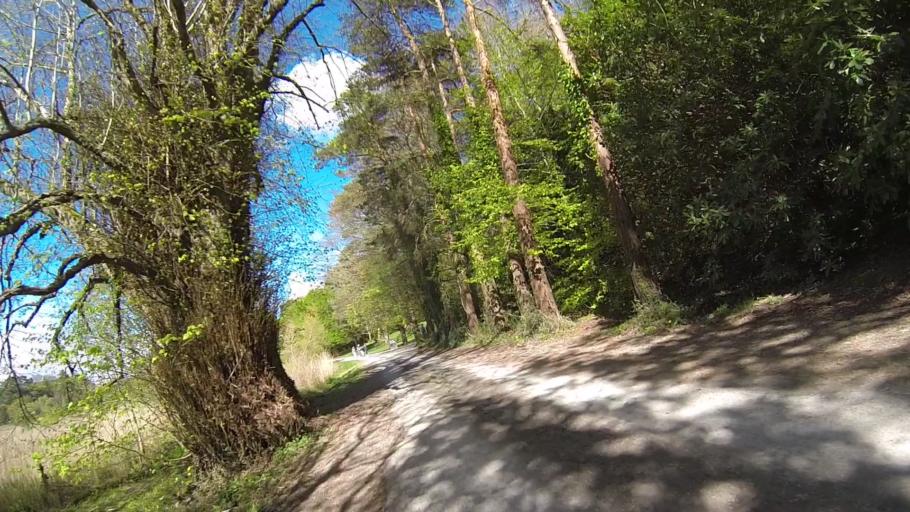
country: IE
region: Munster
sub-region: Ciarrai
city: Cill Airne
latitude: 52.0144
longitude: -9.5068
